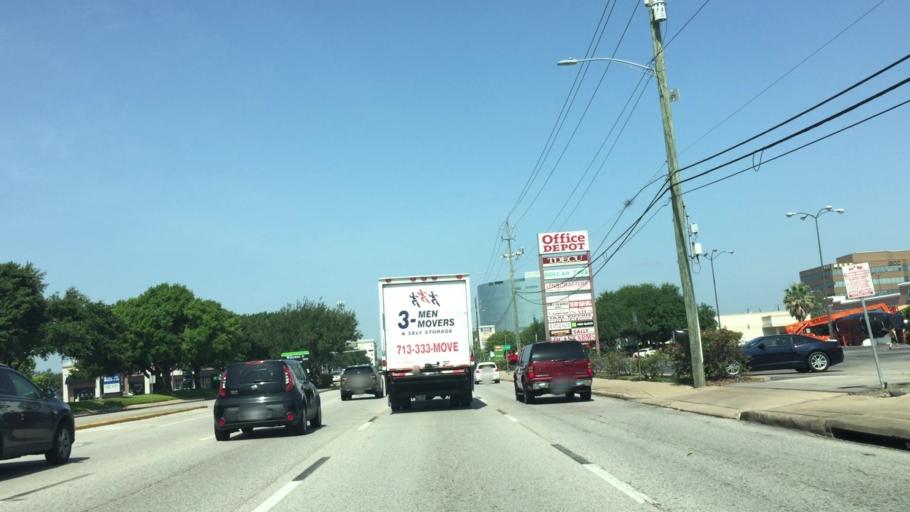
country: US
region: Texas
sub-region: Harris County
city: Bunker Hill Village
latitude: 29.7369
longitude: -95.5691
